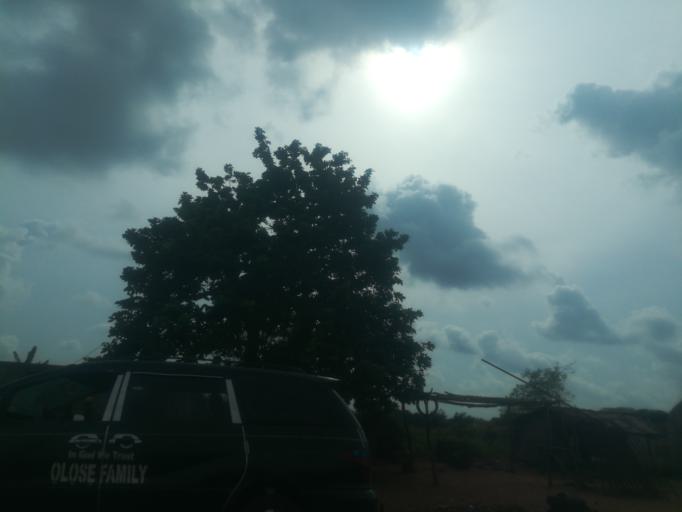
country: NG
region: Ogun
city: Ayetoro
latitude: 7.3935
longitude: 3.0126
